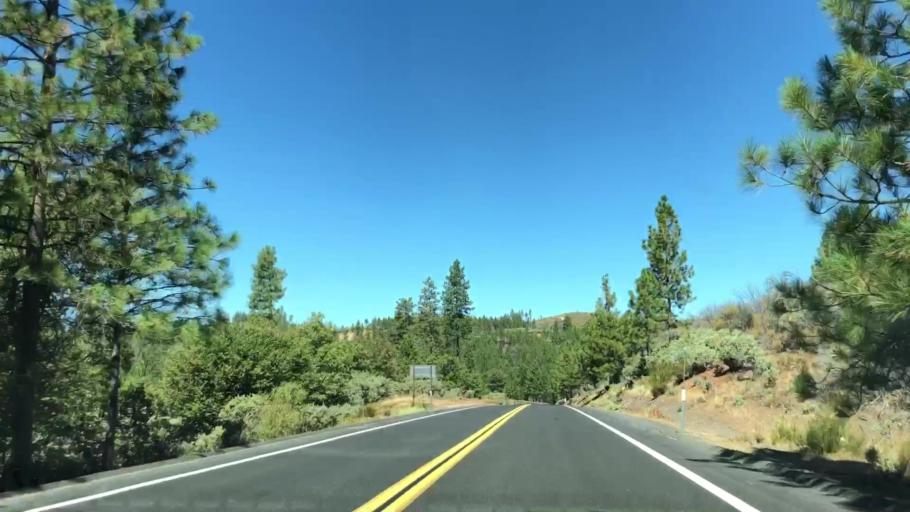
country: US
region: California
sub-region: Tuolumne County
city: Tuolumne City
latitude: 37.8163
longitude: -120.0727
